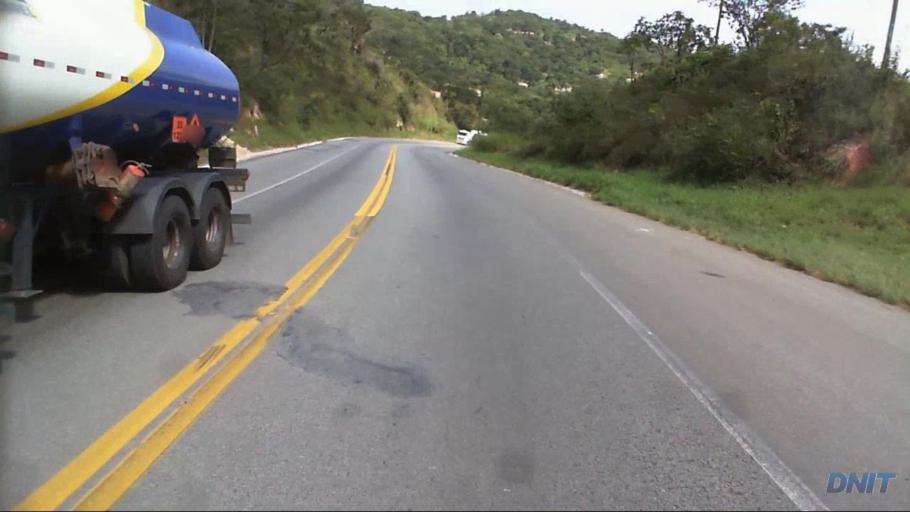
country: BR
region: Minas Gerais
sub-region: Santa Luzia
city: Santa Luzia
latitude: -19.8189
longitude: -43.8116
